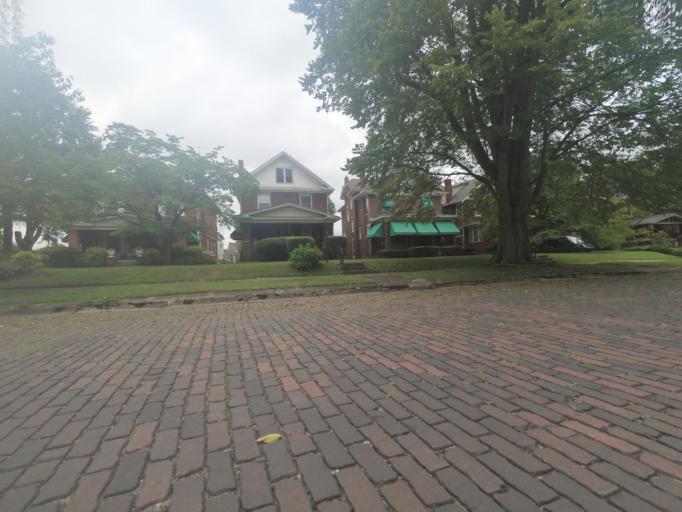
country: US
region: West Virginia
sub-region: Cabell County
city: Huntington
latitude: 38.4113
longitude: -82.4475
